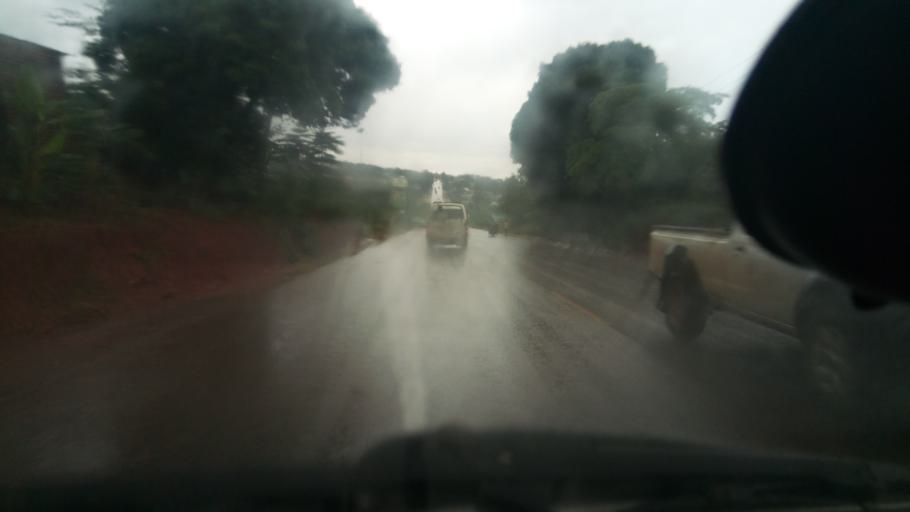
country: UG
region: Central Region
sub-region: Wakiso District
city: Wakiso
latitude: 0.4086
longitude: 32.4661
